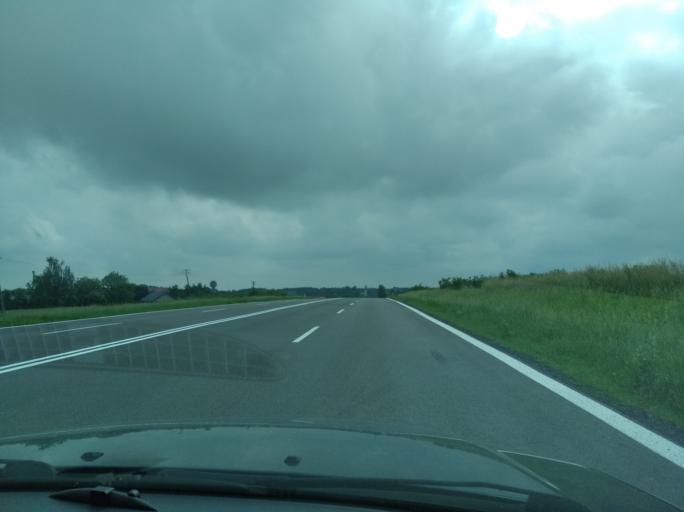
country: PL
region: Subcarpathian Voivodeship
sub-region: Powiat przeworski
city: Rozborz
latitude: 50.0468
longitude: 22.5397
